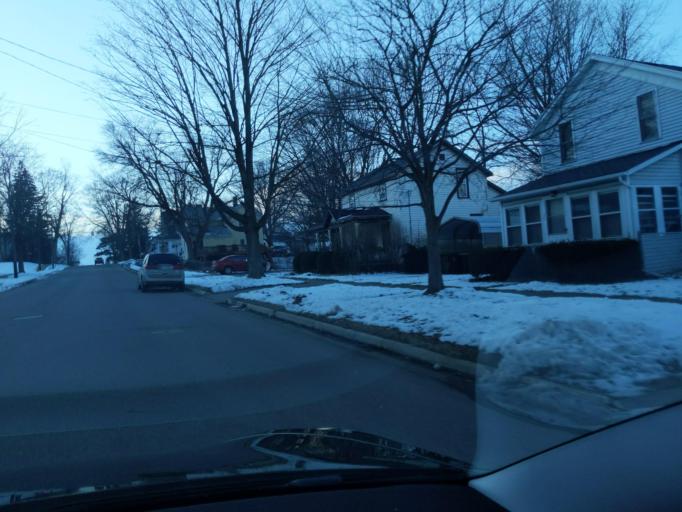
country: US
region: Michigan
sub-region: Ingham County
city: Mason
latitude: 42.5803
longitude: -84.4385
